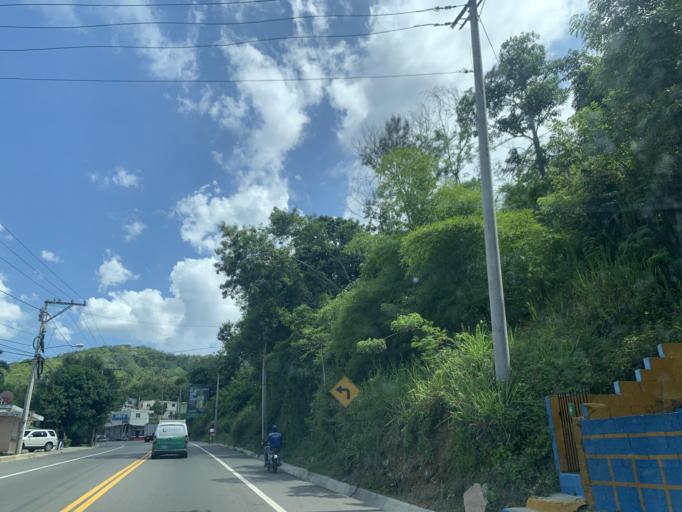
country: DO
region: Puerto Plata
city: Altamira
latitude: 19.6747
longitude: -70.8354
